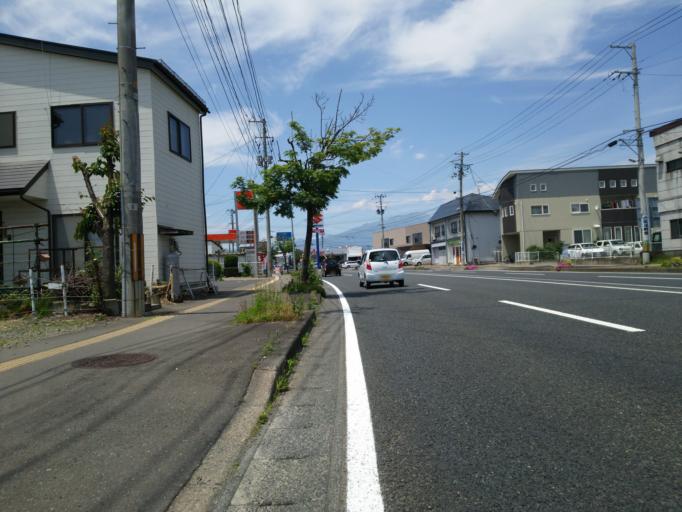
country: JP
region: Iwate
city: Morioka-shi
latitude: 39.7069
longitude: 141.1207
